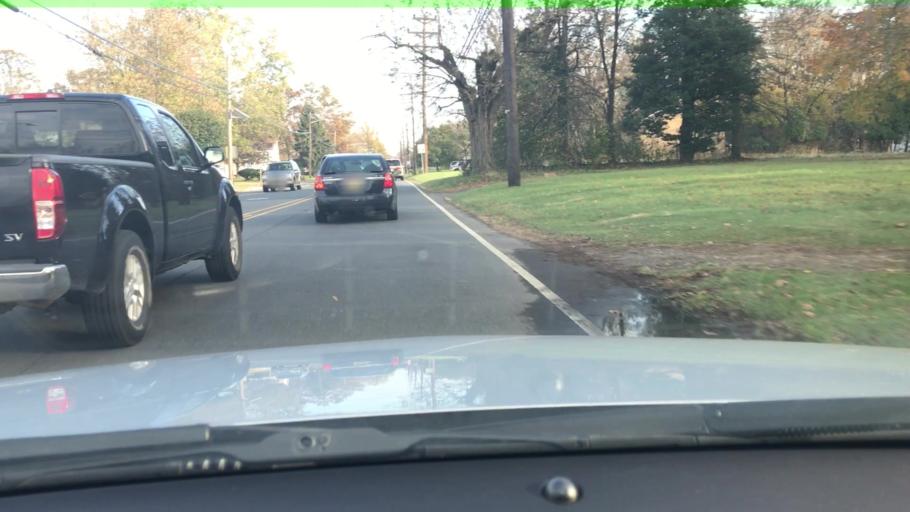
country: US
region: New Jersey
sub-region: Mercer County
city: Mercerville
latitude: 40.2243
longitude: -74.6861
